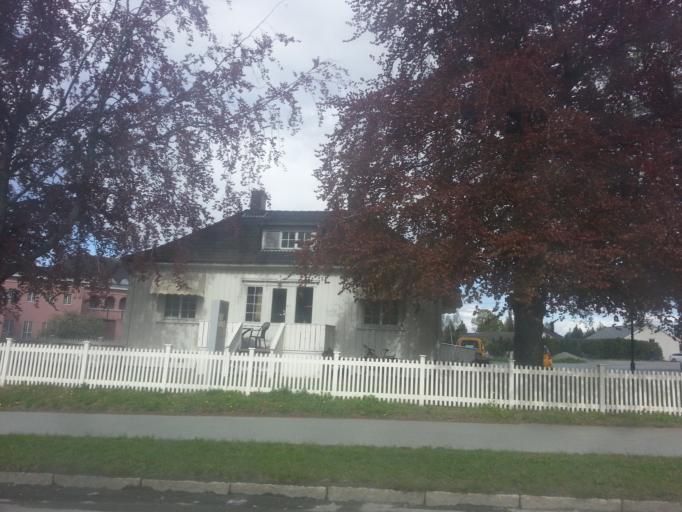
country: NO
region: Sor-Trondelag
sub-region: Trondheim
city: Trondheim
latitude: 63.4105
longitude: 10.4357
